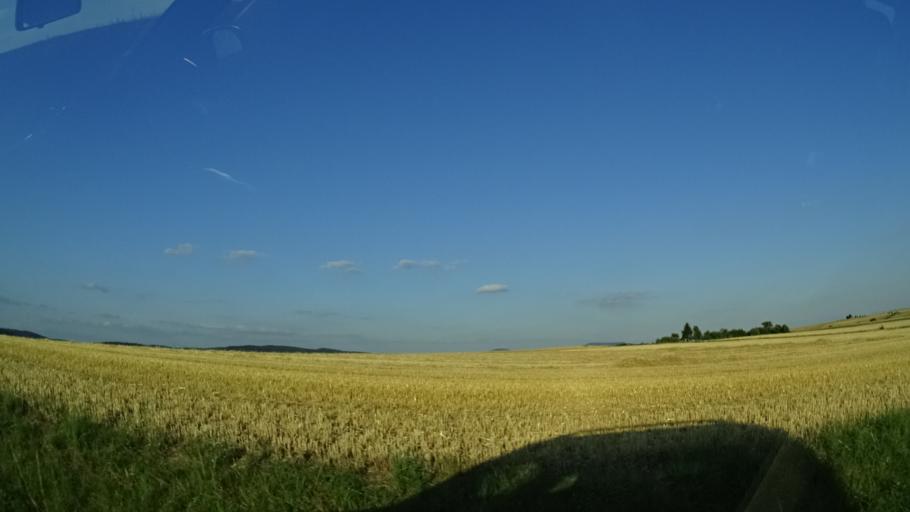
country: DE
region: Thuringia
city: Wolfershausen
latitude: 50.4436
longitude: 10.4004
